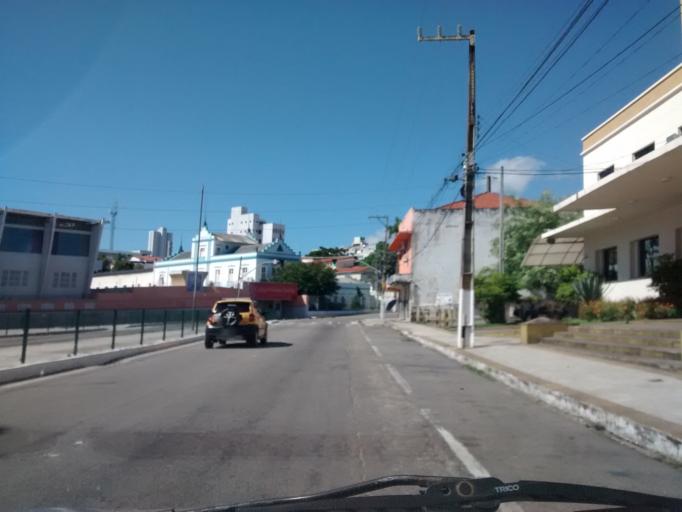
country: BR
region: Rio Grande do Norte
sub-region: Natal
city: Natal
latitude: -5.7801
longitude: -35.2060
